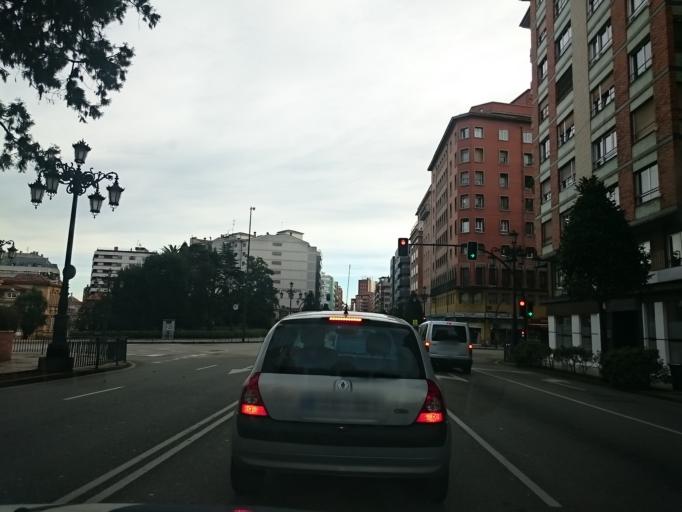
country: ES
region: Asturias
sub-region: Province of Asturias
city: Oviedo
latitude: 43.3636
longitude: -5.8584
